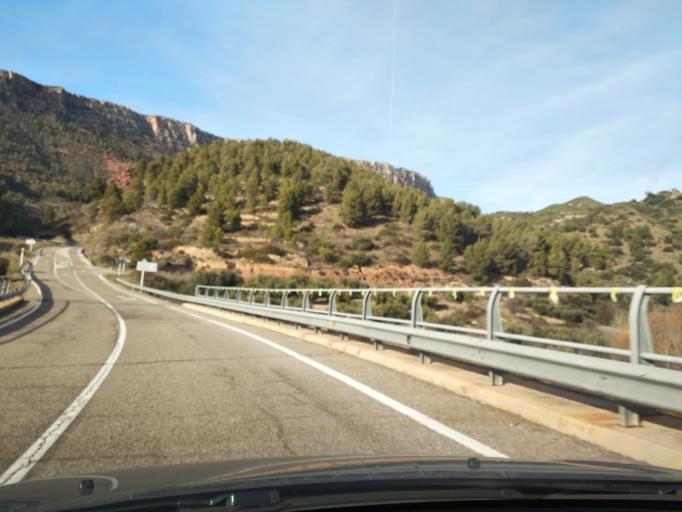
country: ES
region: Catalonia
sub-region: Provincia de Tarragona
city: Margalef
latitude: 41.2216
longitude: 0.7643
